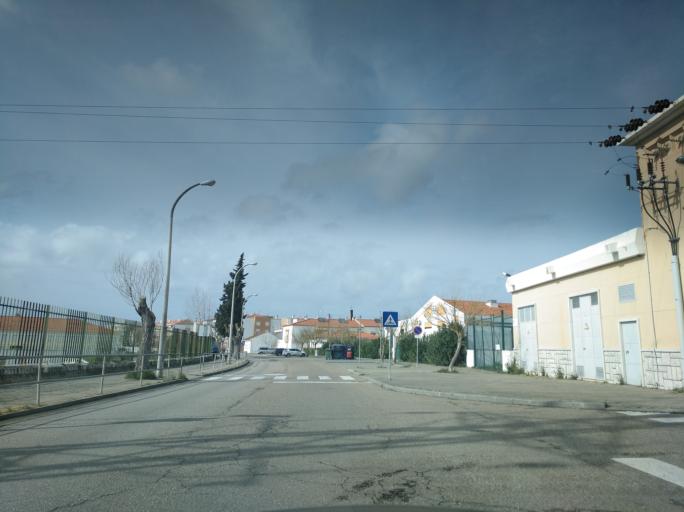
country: PT
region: Setubal
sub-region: Grandola
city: Grandola
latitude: 38.1723
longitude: -8.5590
